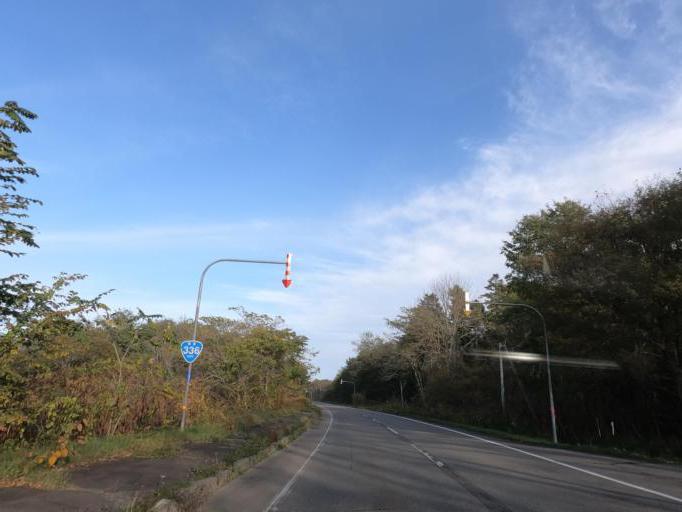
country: JP
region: Hokkaido
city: Obihiro
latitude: 42.5008
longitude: 143.4099
